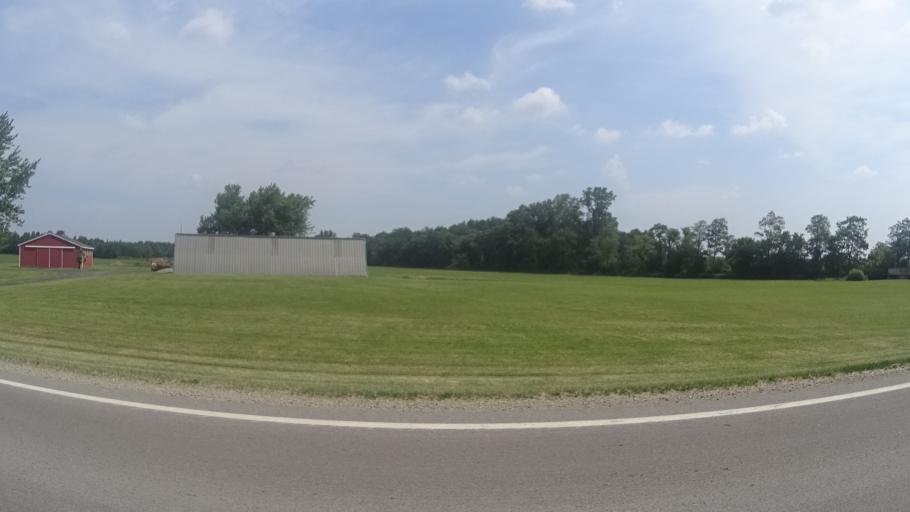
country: US
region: Ohio
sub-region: Erie County
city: Sandusky
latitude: 41.3521
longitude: -82.7018
